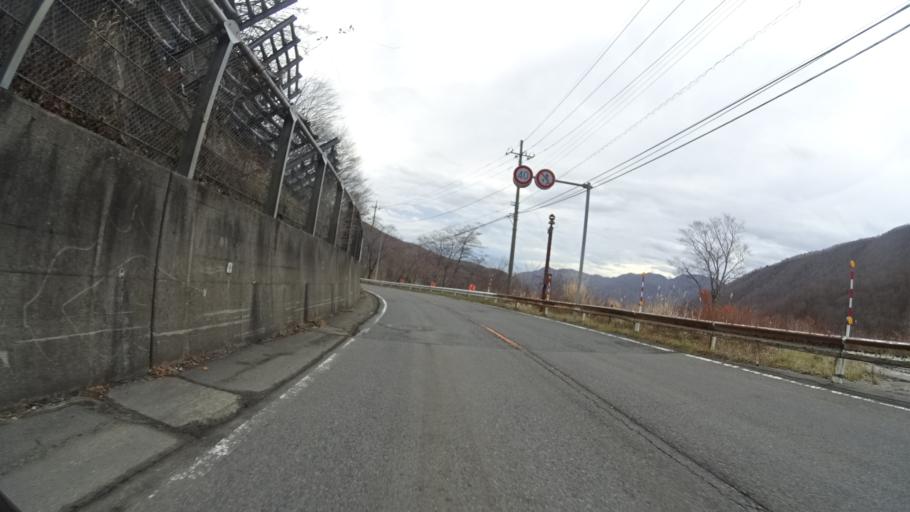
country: JP
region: Gunma
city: Nakanojomachi
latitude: 36.7603
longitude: 138.8281
